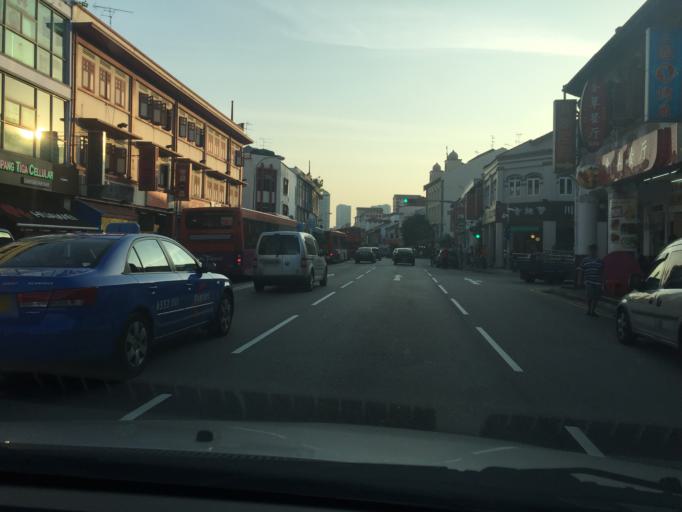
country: SG
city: Singapore
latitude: 1.3124
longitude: 103.8780
